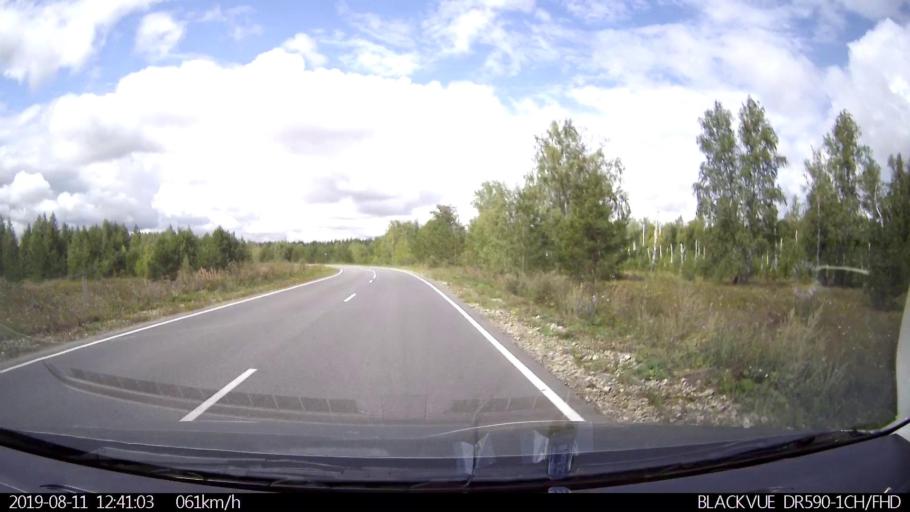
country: RU
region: Ulyanovsk
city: Ignatovka
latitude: 53.8420
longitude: 47.7720
